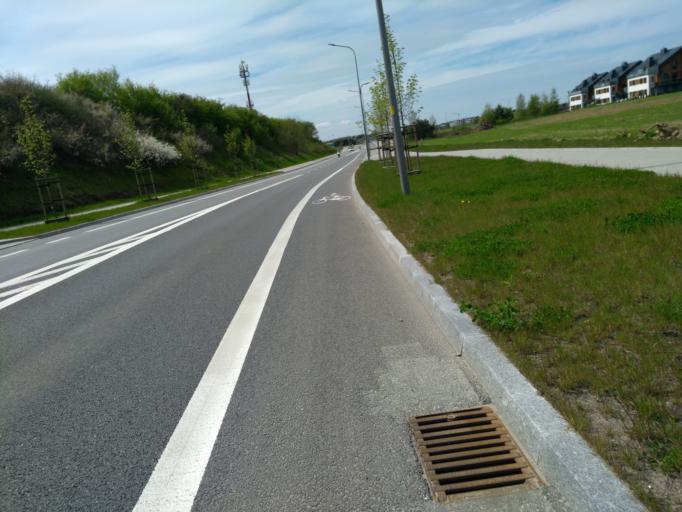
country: PL
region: Pomeranian Voivodeship
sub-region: Gdynia
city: Wielki Kack
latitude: 54.4165
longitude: 18.4726
